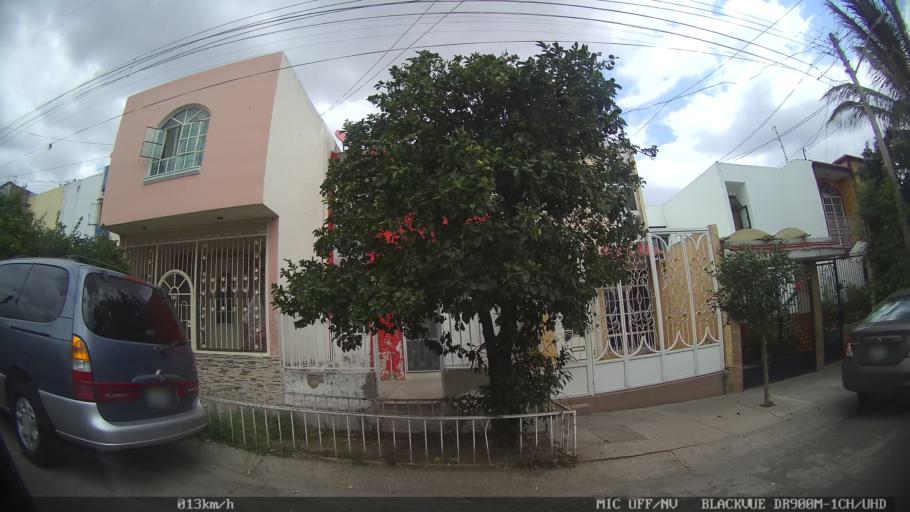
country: MX
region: Jalisco
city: Tonala
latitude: 20.6296
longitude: -103.2598
